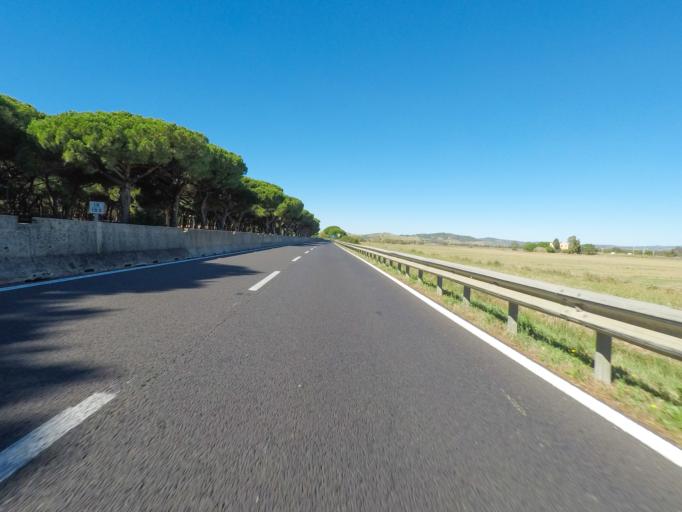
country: IT
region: Tuscany
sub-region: Provincia di Grosseto
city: Albinia
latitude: 42.5299
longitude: 11.1876
